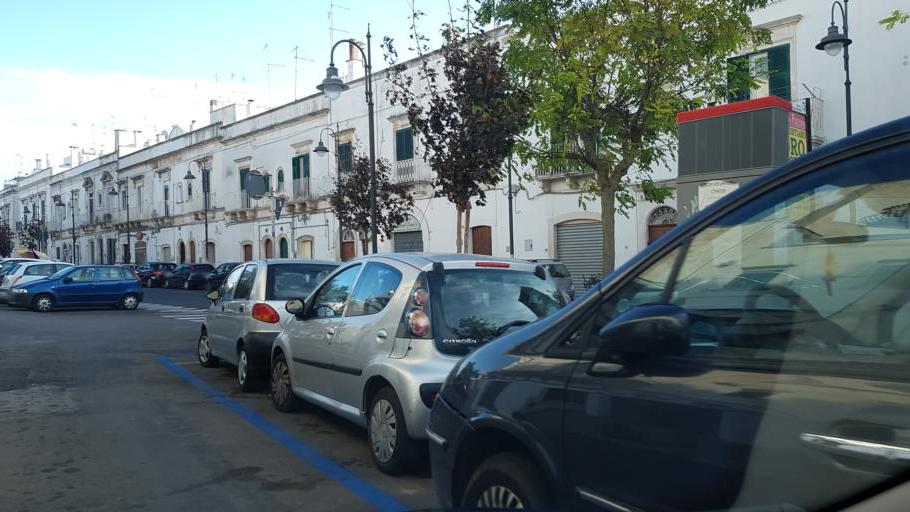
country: IT
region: Apulia
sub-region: Provincia di Taranto
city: Martina Franca
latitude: 40.7043
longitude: 17.3346
